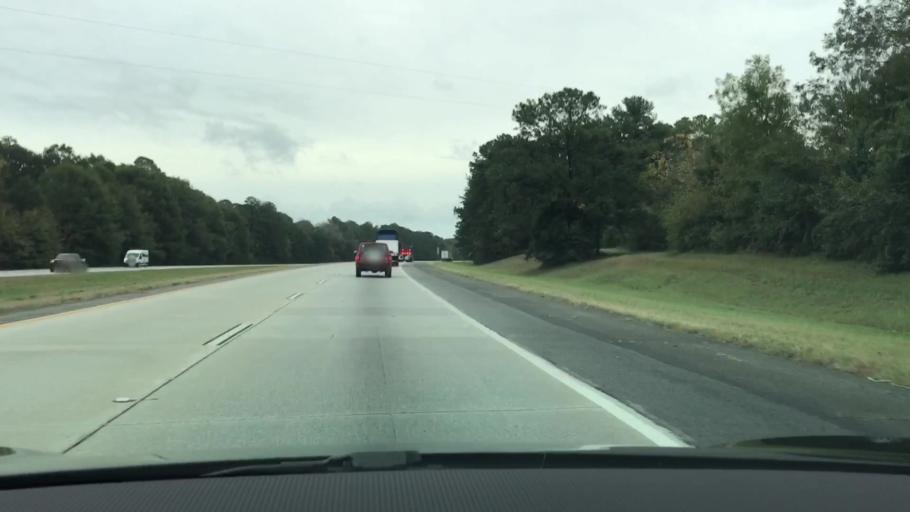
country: US
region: Georgia
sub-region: Taliaferro County
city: Crawfordville
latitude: 33.5379
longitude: -83.0001
